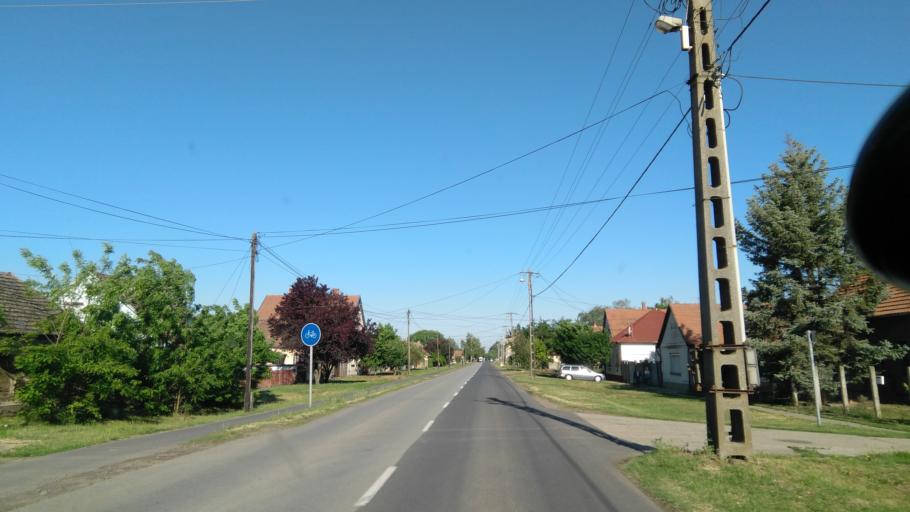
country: HU
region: Bekes
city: Elek
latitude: 46.5317
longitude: 21.2442
